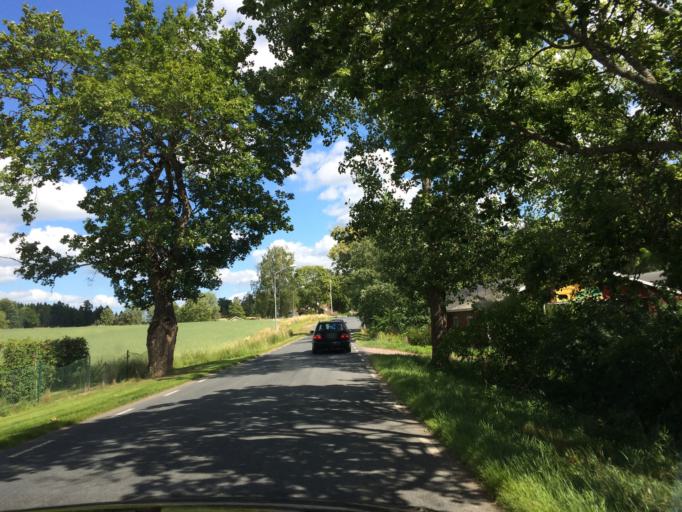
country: SE
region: Soedermanland
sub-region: Katrineholms Kommun
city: Katrineholm
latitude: 59.0669
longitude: 16.3561
